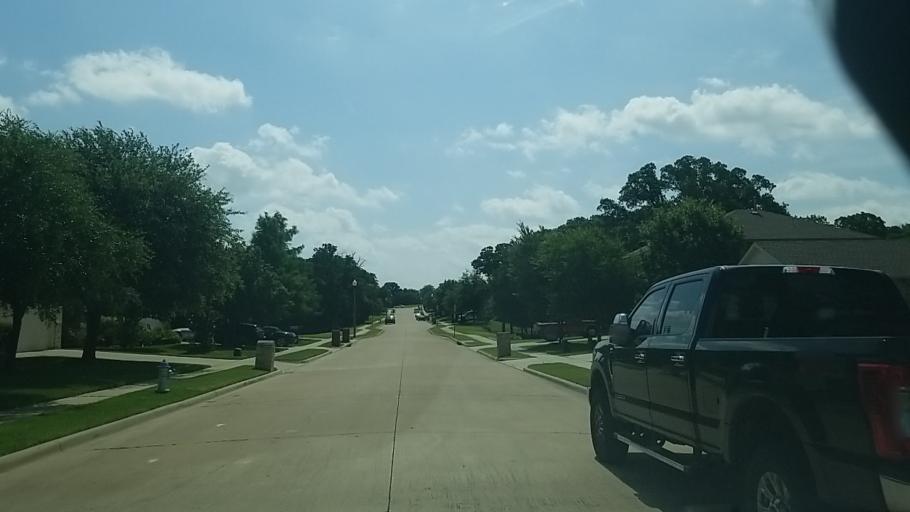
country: US
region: Texas
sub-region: Denton County
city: Corinth
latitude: 33.1435
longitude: -97.1005
